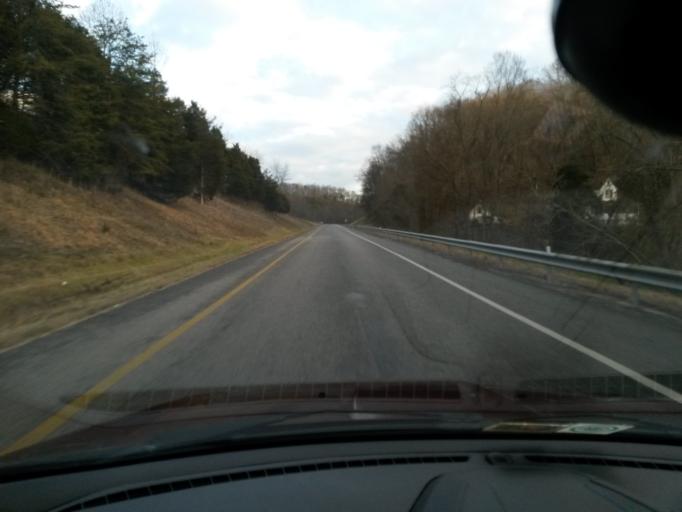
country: US
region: Virginia
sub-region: City of Covington
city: Covington
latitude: 37.8079
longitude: -80.0612
